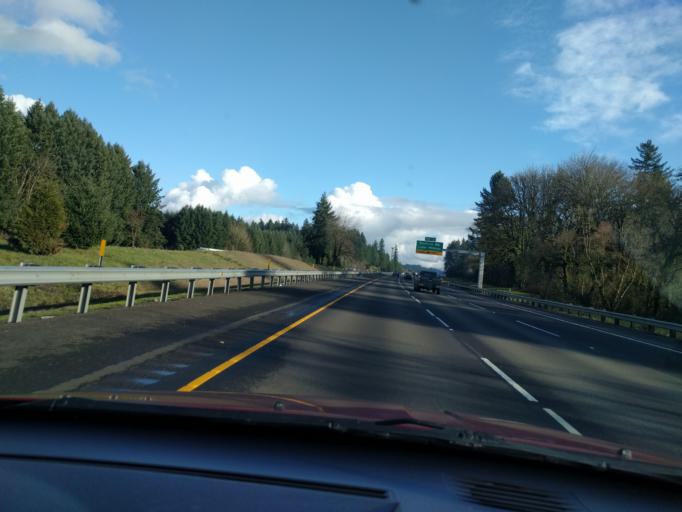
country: US
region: Oregon
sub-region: Clackamas County
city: Stafford
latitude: 45.3731
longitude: -122.7251
